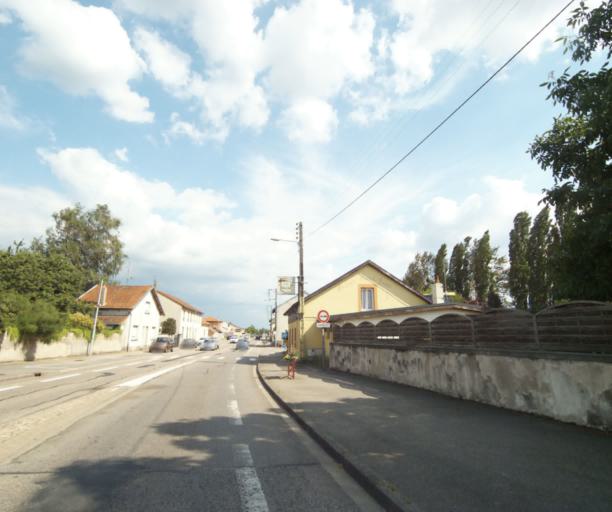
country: FR
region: Lorraine
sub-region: Departement de Meurthe-et-Moselle
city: Chanteheux
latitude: 48.5770
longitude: 6.5249
